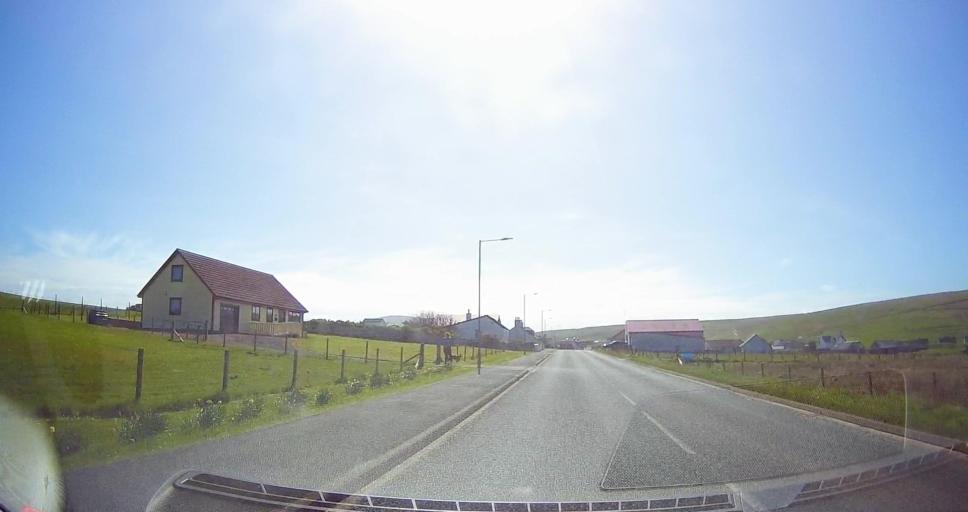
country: GB
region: Scotland
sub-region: Shetland Islands
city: Sandwick
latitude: 60.0006
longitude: -1.2396
